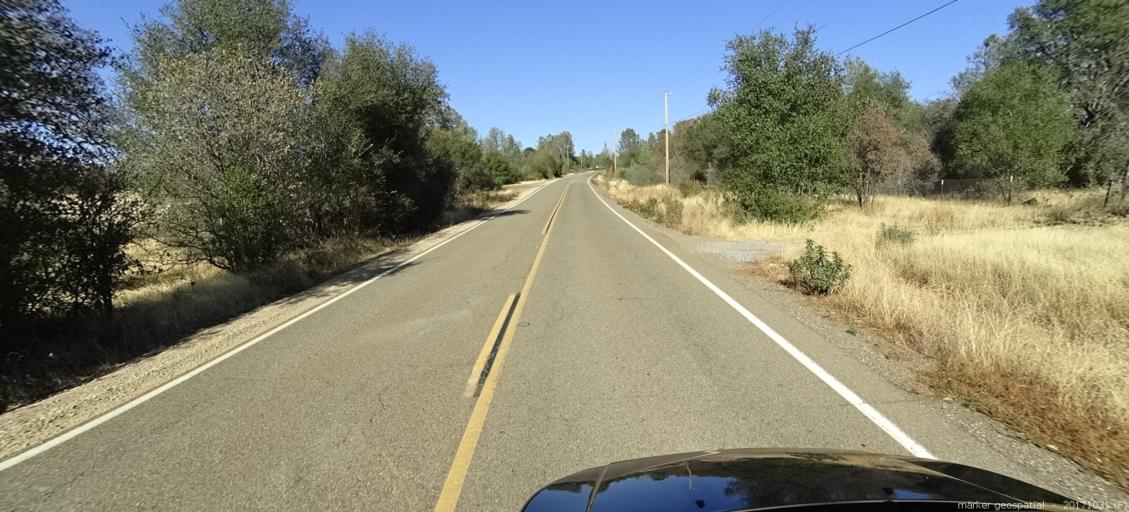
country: US
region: California
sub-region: Shasta County
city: Shingletown
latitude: 40.5072
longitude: -122.0370
